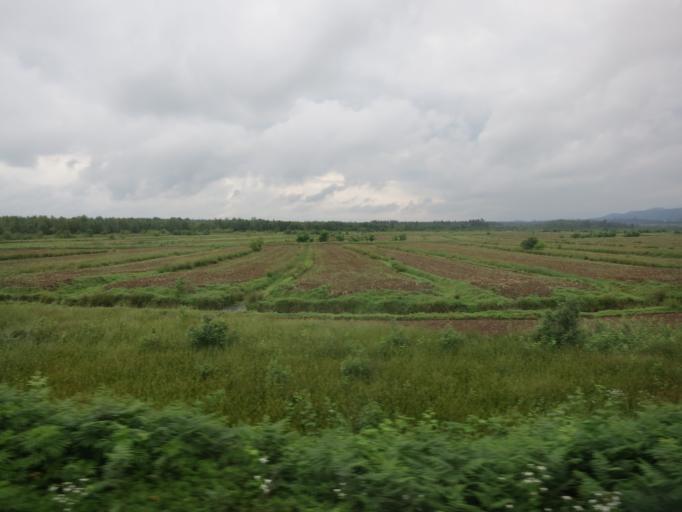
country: GE
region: Ajaria
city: Ochkhamuri
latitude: 41.8776
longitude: 41.8259
